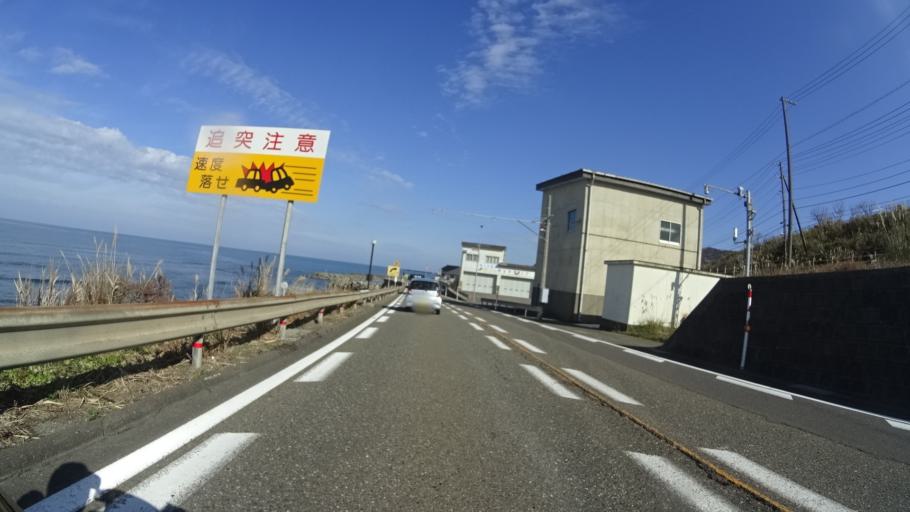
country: JP
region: Niigata
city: Itoigawa
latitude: 37.1186
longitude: 138.0313
